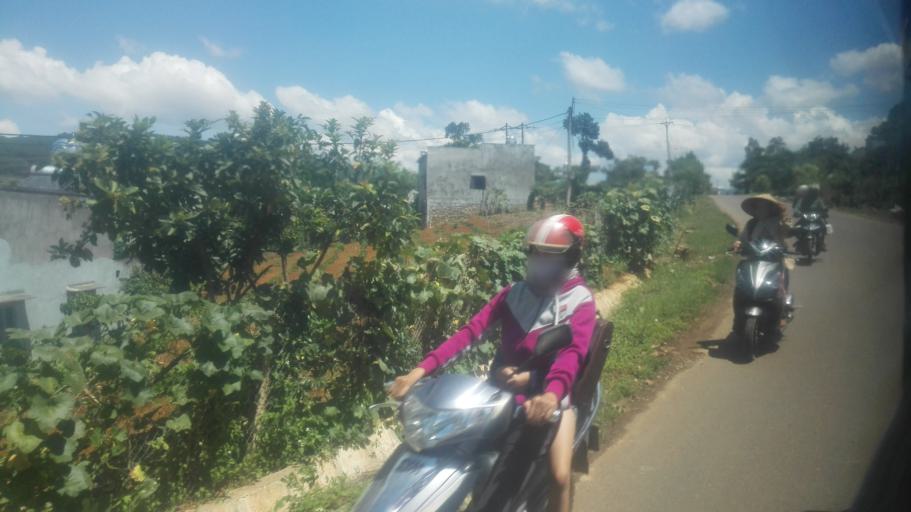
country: VN
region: Lam Dong
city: Da Lat
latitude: 11.8772
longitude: 108.3427
